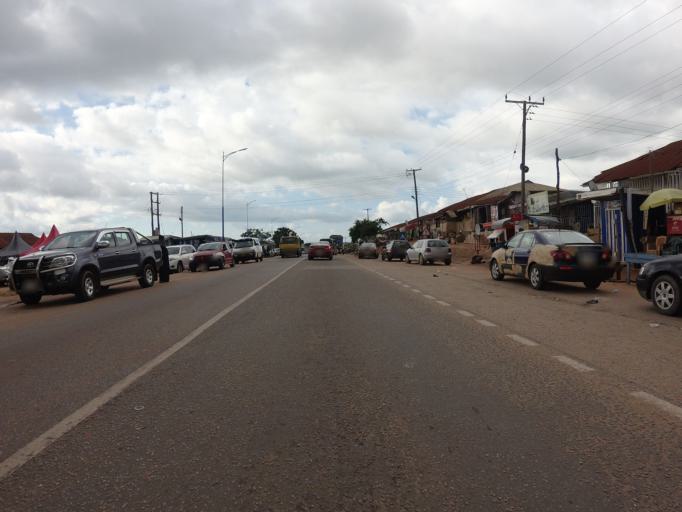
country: GH
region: Ashanti
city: Tafo
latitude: 6.8159
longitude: -1.6483
